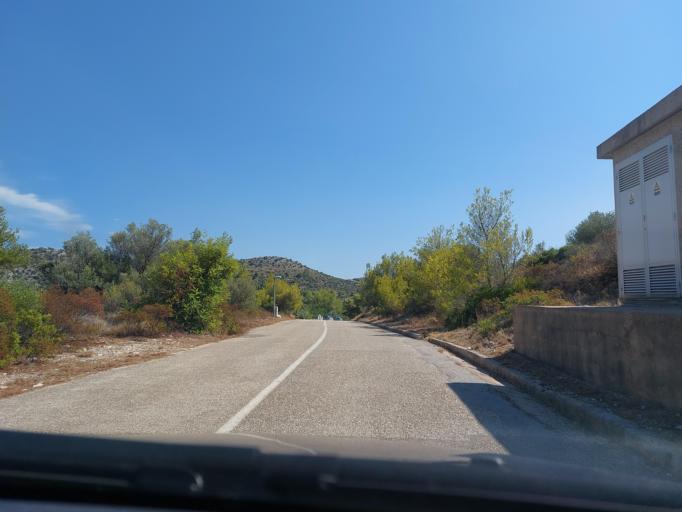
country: HR
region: Dubrovacko-Neretvanska
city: Smokvica
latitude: 42.7362
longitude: 16.8849
